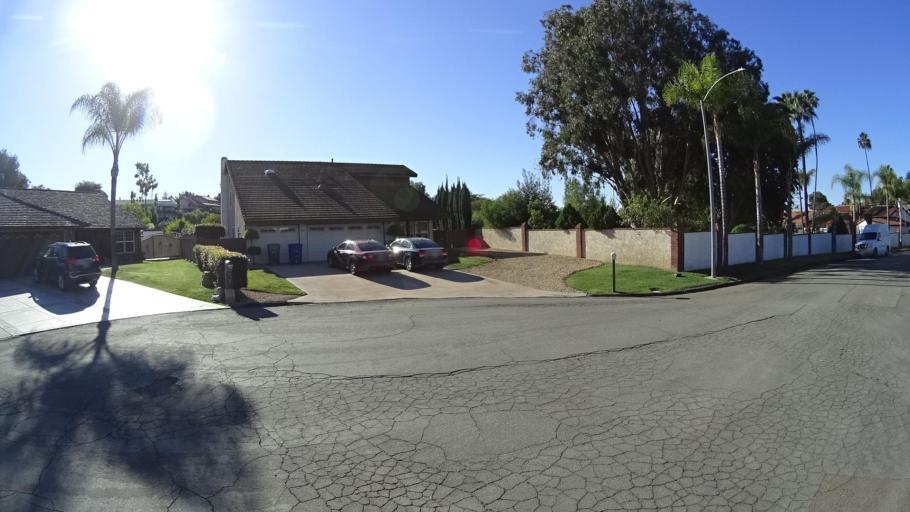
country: US
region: California
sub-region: San Diego County
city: Bonita
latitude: 32.6827
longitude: -117.0241
